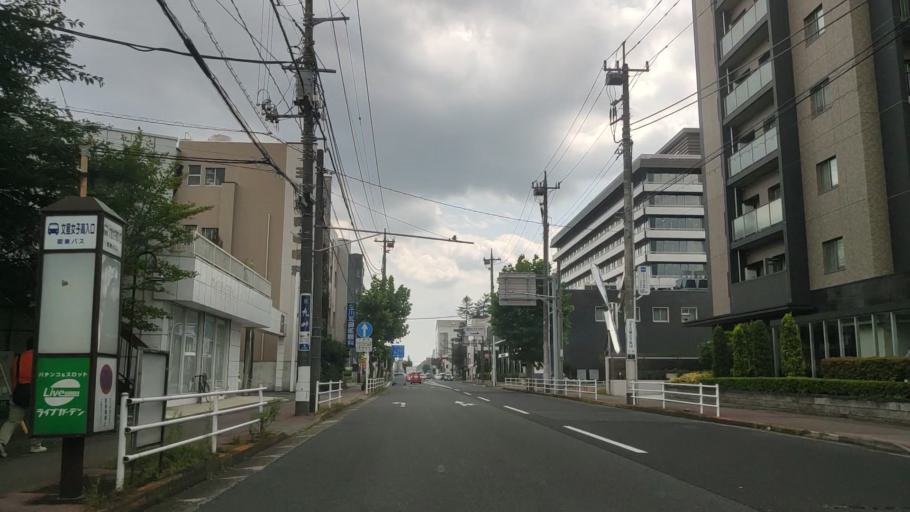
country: JP
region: Tochigi
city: Utsunomiya-shi
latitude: 36.5669
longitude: 139.8683
